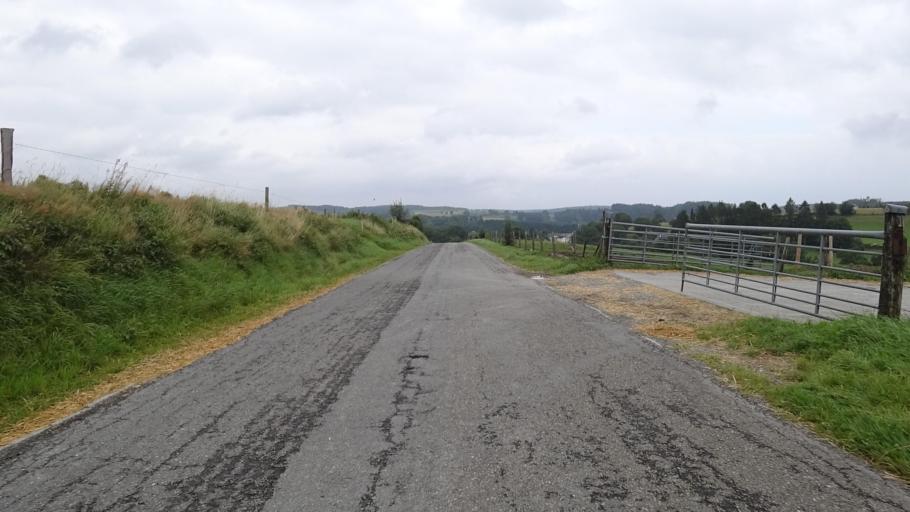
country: BE
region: Wallonia
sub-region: Province du Luxembourg
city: Chiny
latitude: 49.8058
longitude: 5.3518
